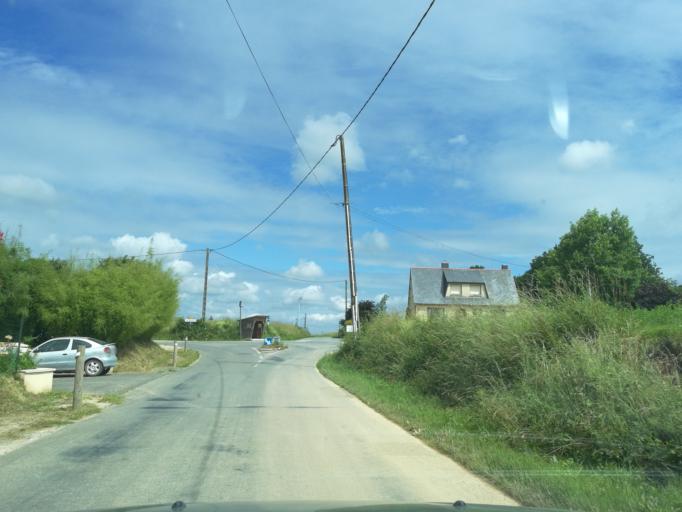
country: FR
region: Brittany
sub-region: Departement d'Ille-et-Vilaine
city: Bedee
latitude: 48.1621
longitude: -1.9725
